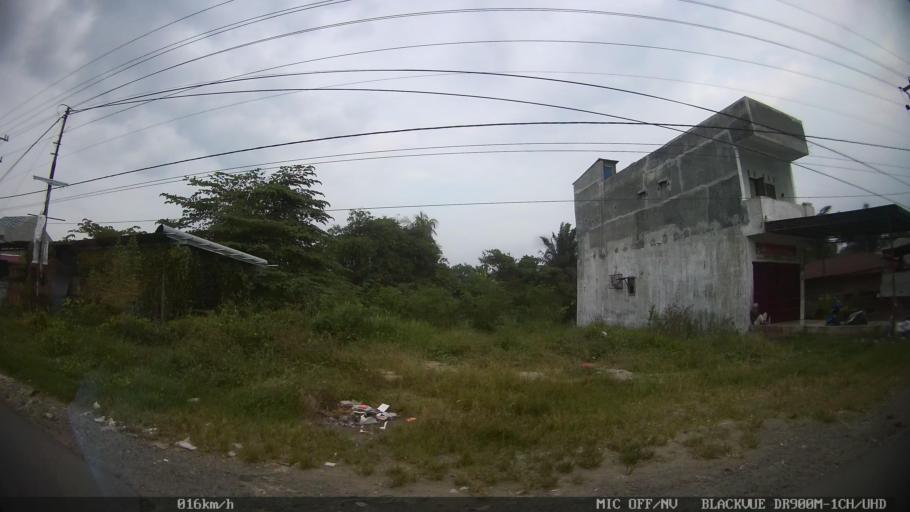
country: ID
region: North Sumatra
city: Sunggal
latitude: 3.5702
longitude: 98.5825
